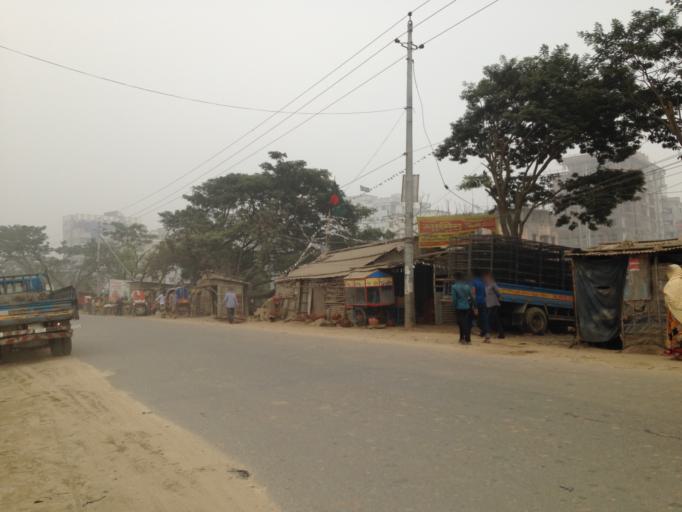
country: BD
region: Dhaka
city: Azimpur
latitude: 23.8006
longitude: 90.3440
